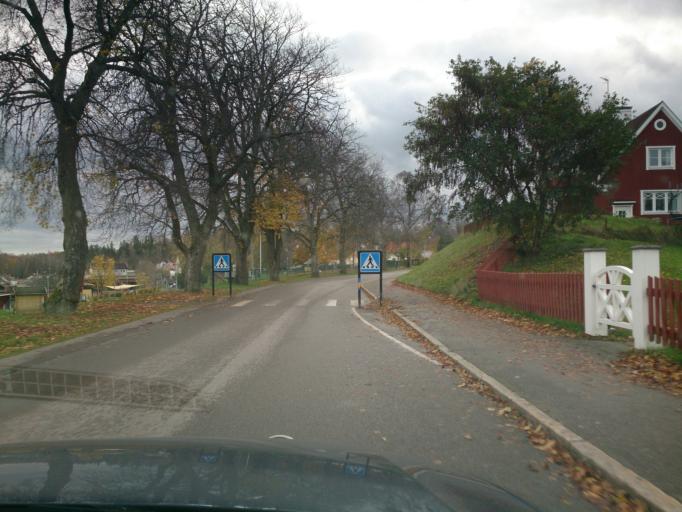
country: SE
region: OEstergoetland
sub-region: Atvidabergs Kommun
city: Atvidaberg
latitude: 58.1951
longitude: 16.0084
